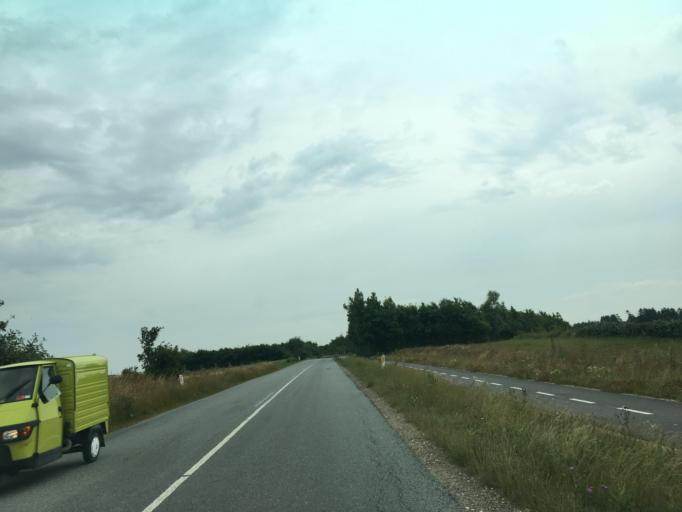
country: DK
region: North Denmark
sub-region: Thisted Kommune
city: Hurup
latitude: 56.8023
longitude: 8.4095
